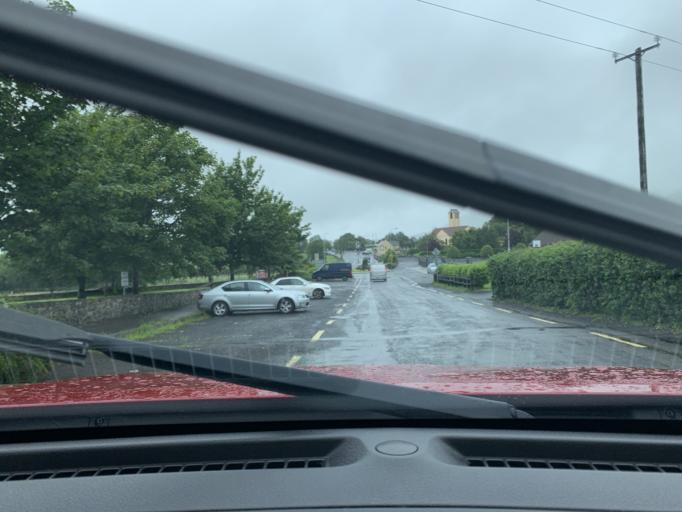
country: IE
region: Connaught
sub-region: Sligo
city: Sligo
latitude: 54.3160
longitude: -8.4791
